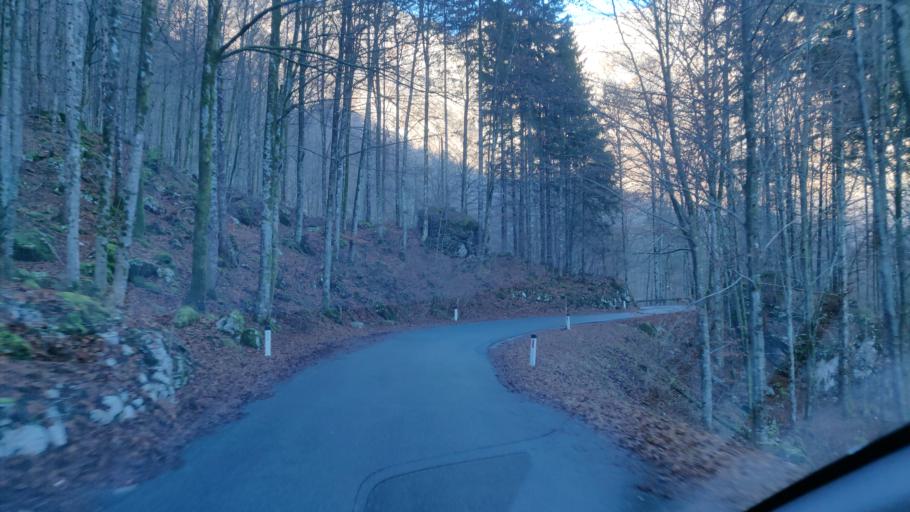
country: SI
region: Tolmin
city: Tolmin
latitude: 46.2783
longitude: 13.8117
